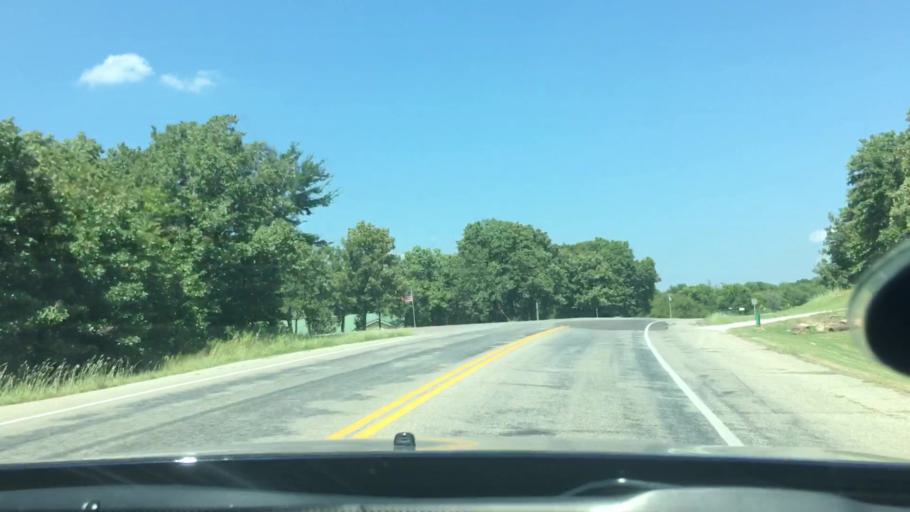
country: US
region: Oklahoma
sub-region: Pontotoc County
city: Byng
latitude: 34.8512
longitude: -96.6784
